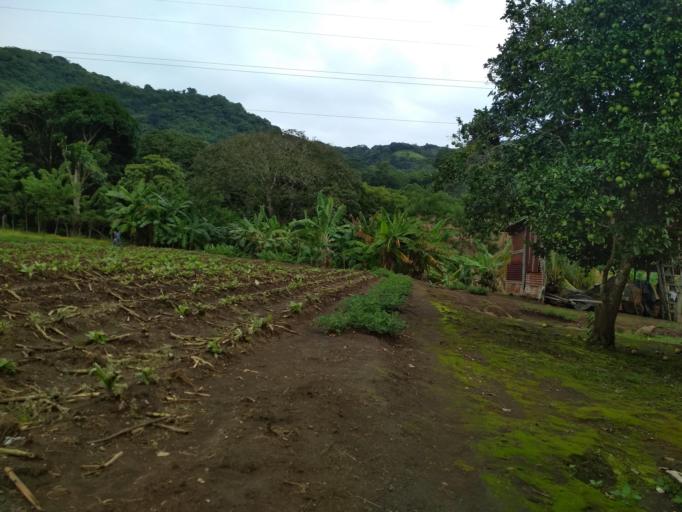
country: MX
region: Veracruz
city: Comoapan
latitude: 18.4092
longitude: -95.1534
